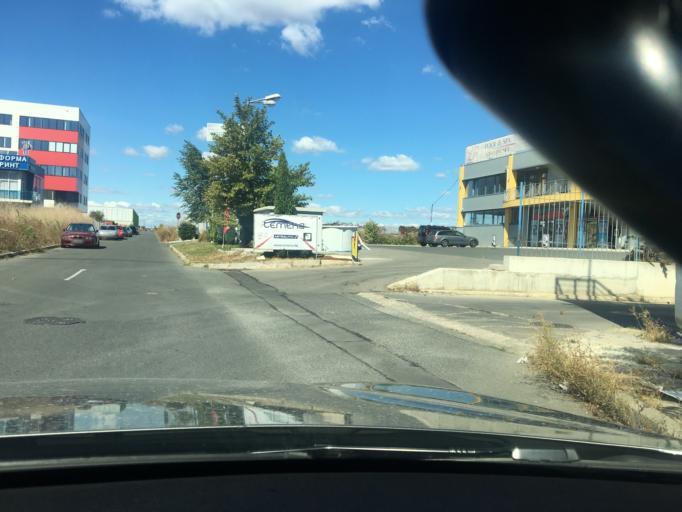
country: BG
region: Burgas
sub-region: Obshtina Burgas
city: Burgas
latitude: 42.5313
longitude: 27.4557
